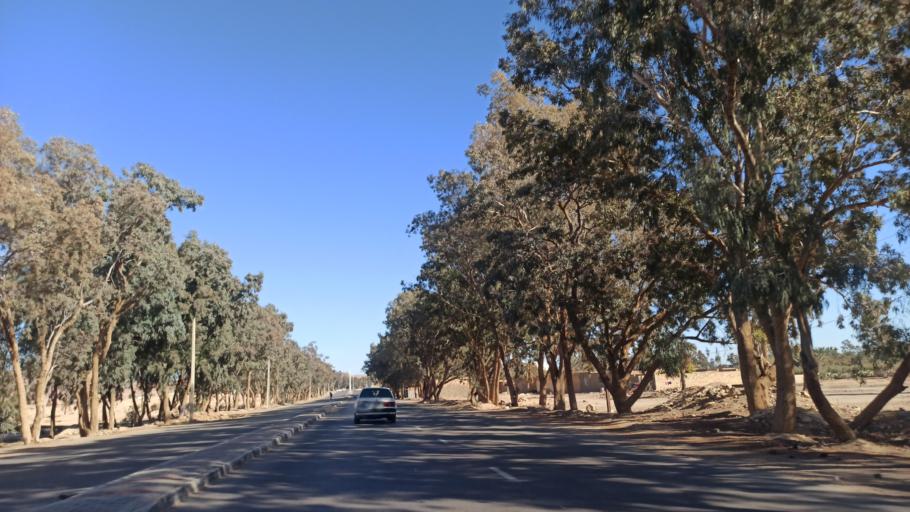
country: TN
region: Gafsa
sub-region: Gafsa Municipality
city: Gafsa
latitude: 34.3979
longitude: 8.7201
